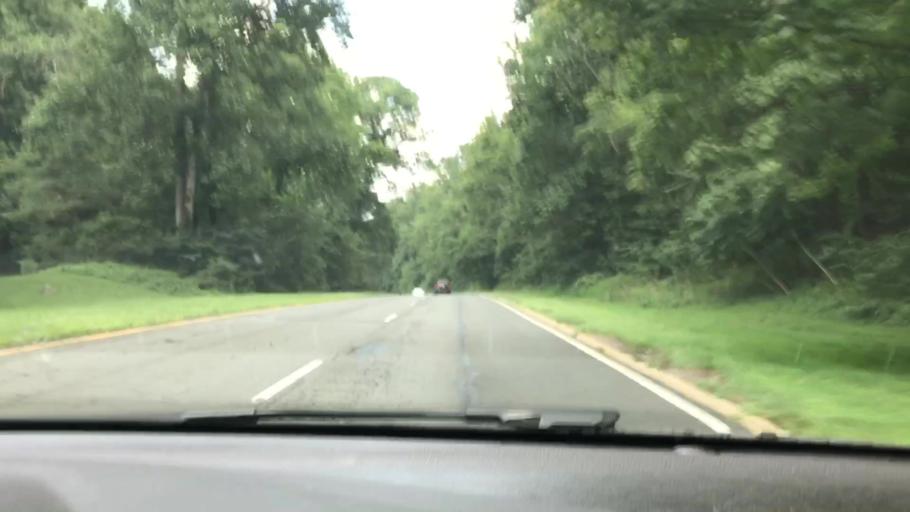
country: US
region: Maryland
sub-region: Montgomery County
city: Brookmont
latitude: 38.9502
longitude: -77.1372
